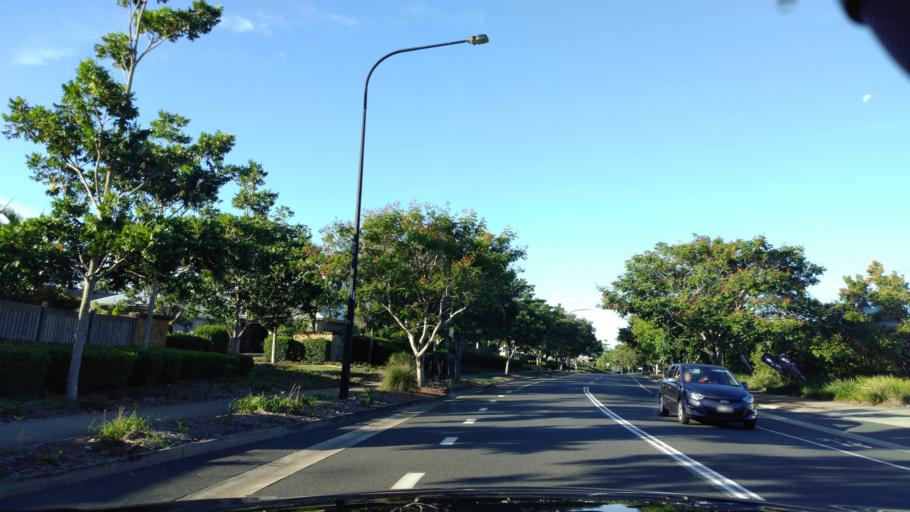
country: AU
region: Queensland
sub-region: Moreton Bay
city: Deception Bay
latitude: -27.2157
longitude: 153.0217
